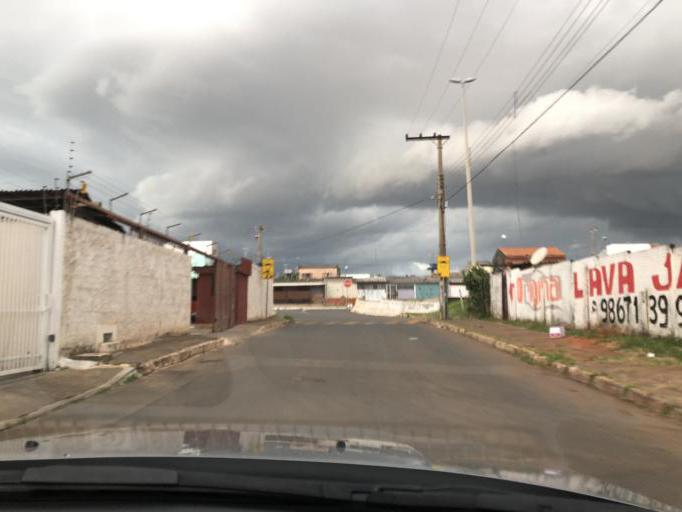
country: BR
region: Federal District
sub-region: Brasilia
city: Brasilia
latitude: -15.8248
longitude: -48.1110
